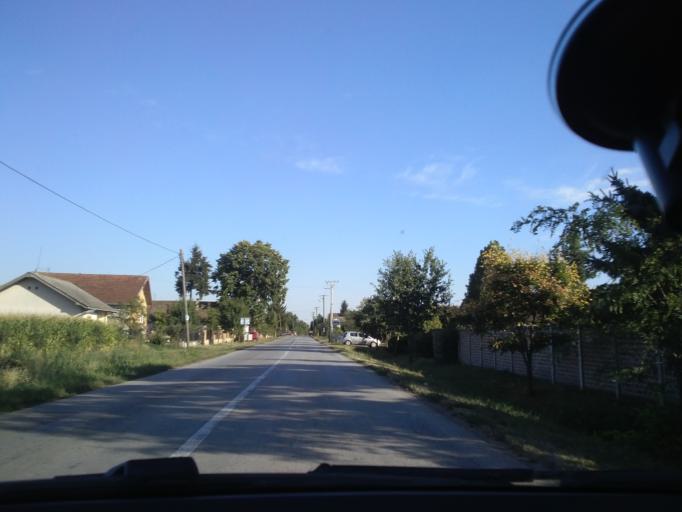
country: RS
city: Doroslovo
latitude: 45.5674
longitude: 19.1948
